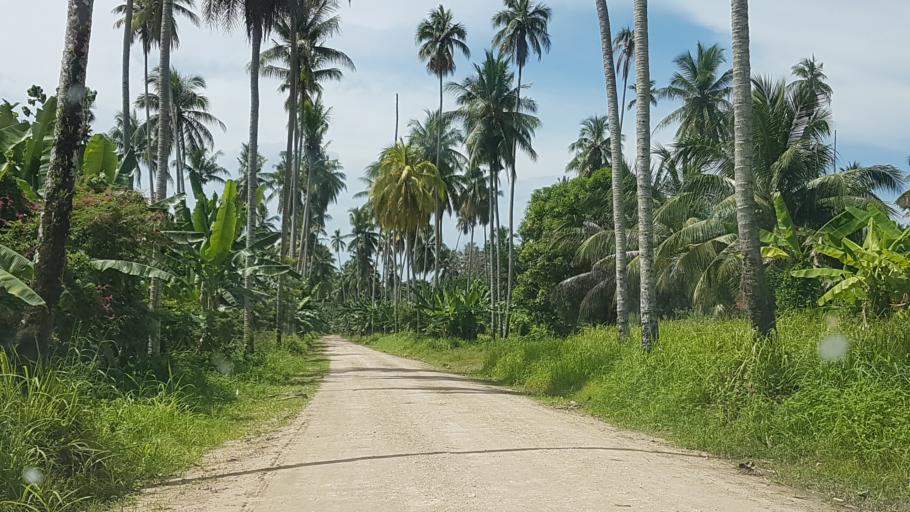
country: PG
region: East Sepik
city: Angoram
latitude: -4.2225
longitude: 144.9317
